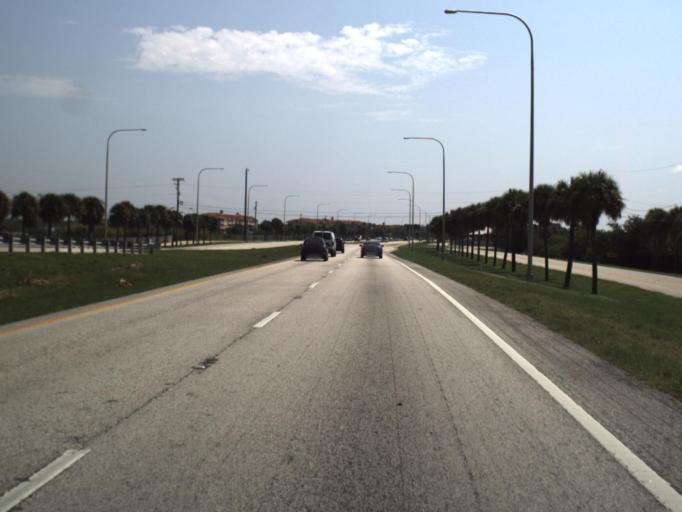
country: US
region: Florida
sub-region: Pinellas County
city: Gandy
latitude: 27.8911
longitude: -82.5399
